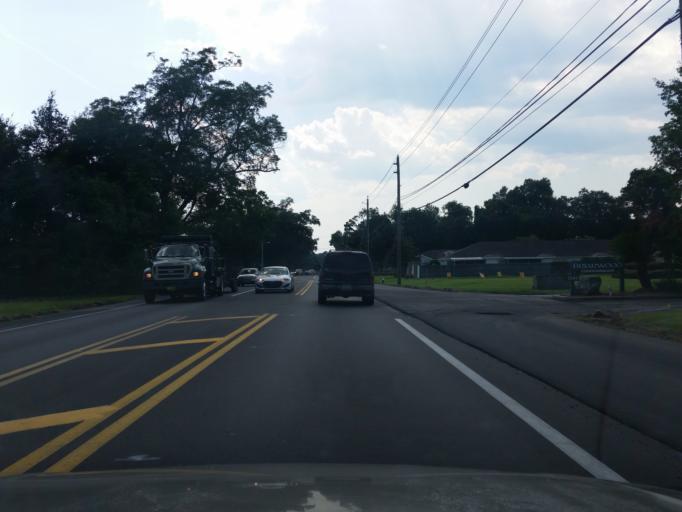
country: US
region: Florida
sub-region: Escambia County
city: Ferry Pass
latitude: 30.5109
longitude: -87.2344
